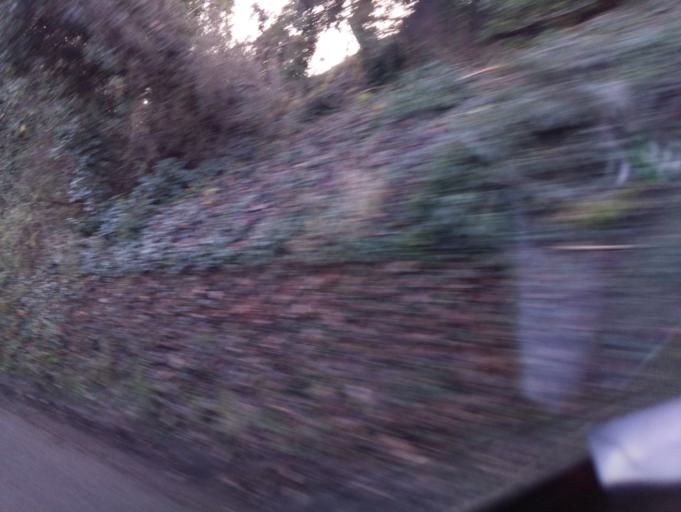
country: GB
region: England
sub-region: Staffordshire
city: Barton under Needwood
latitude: 52.7929
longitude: -1.7036
